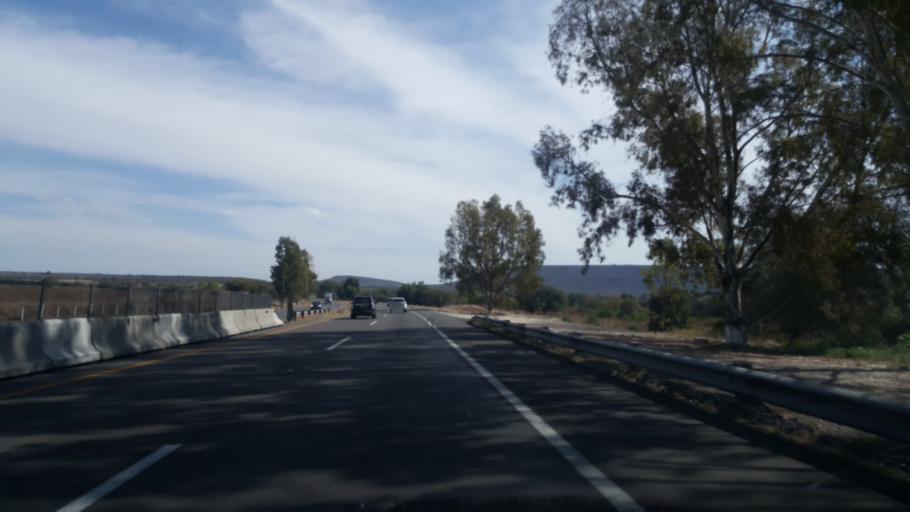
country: MX
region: Jalisco
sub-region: Lagos de Moreno
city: Cristeros [Fraccionamiento]
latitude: 21.2842
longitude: -101.9990
